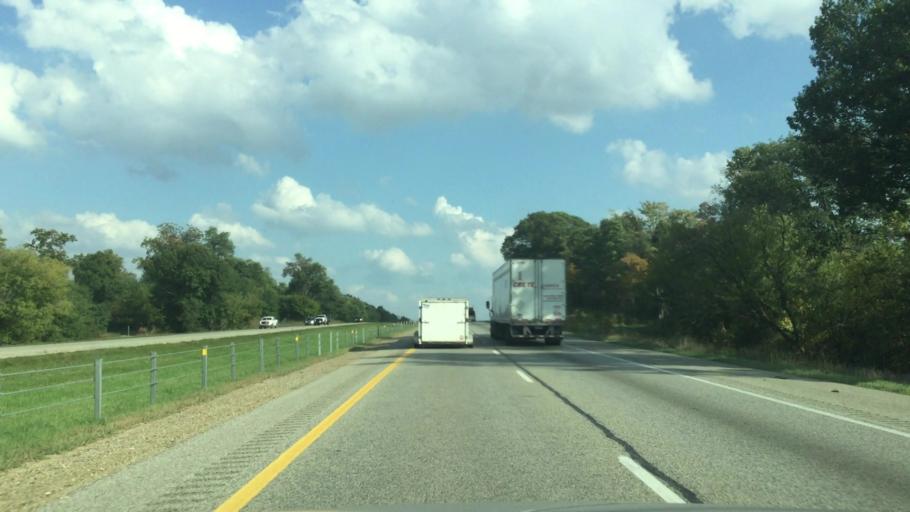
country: US
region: Michigan
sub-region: Kalamazoo County
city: Galesburg
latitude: 42.2784
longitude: -85.3272
